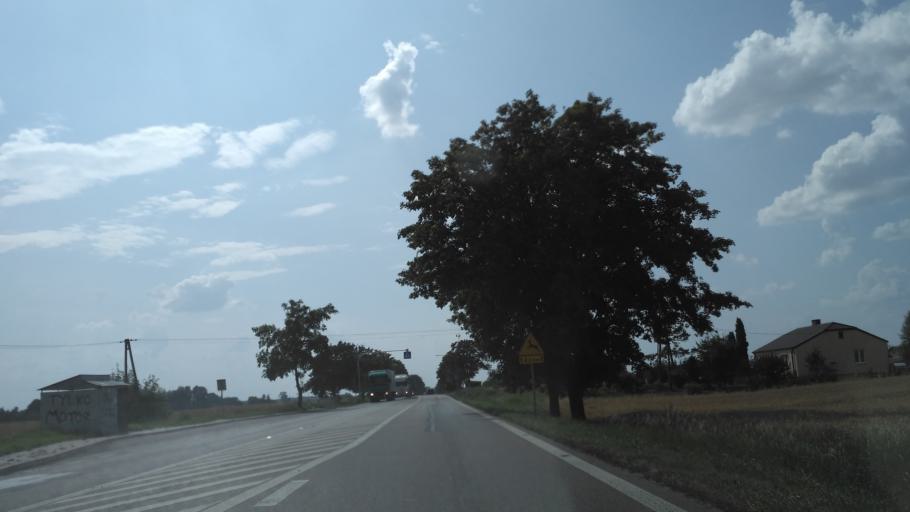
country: PL
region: Lublin Voivodeship
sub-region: Powiat chelmski
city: Rejowiec Fabryczny
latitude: 51.1780
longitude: 23.2007
